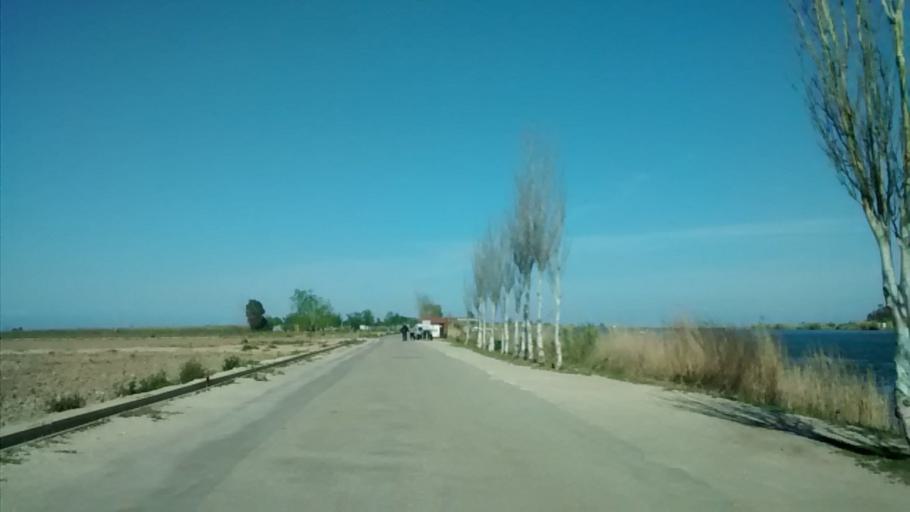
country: ES
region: Catalonia
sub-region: Provincia de Tarragona
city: Deltebre
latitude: 40.7144
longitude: 0.8375
